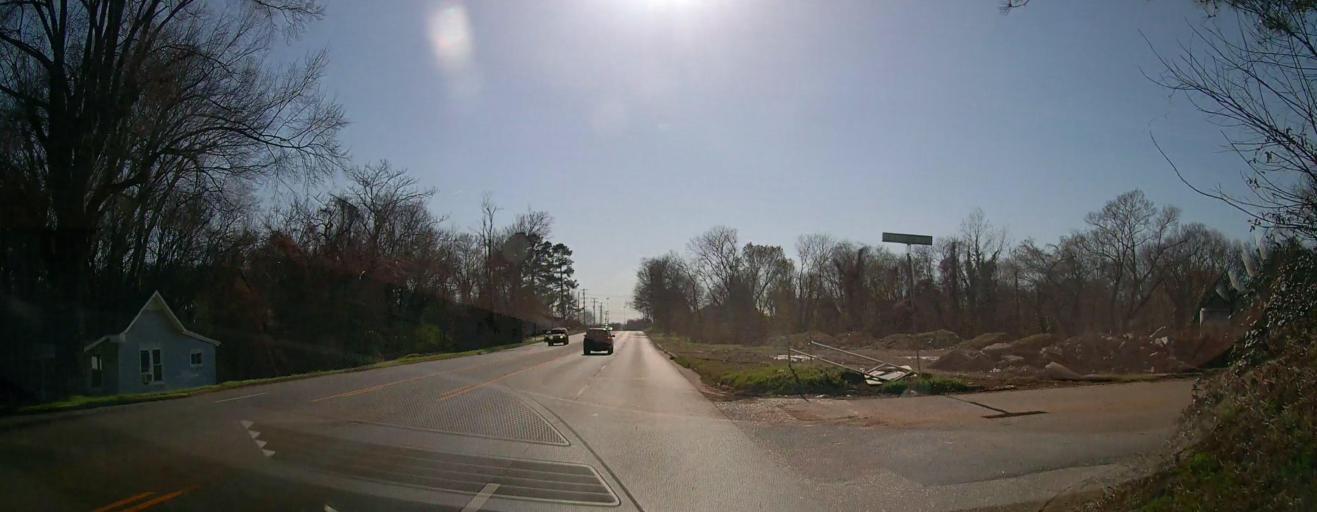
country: US
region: Alabama
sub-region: Lauderdale County
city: East Florence
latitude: 34.8062
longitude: -87.6444
